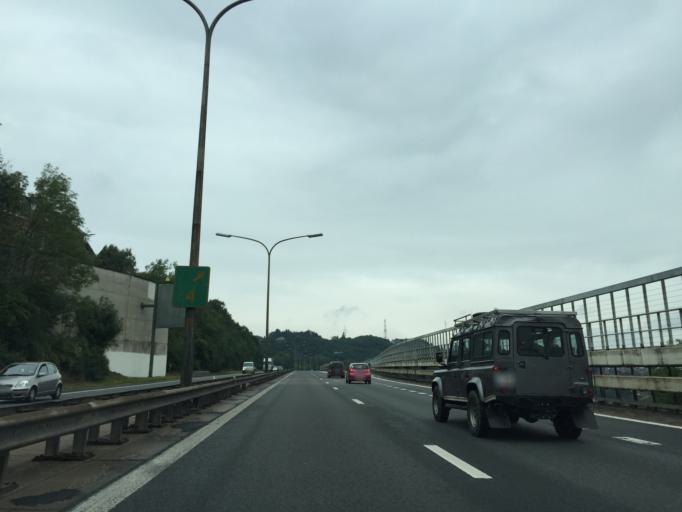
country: BE
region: Wallonia
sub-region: Province de Liege
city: Verviers
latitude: 50.5898
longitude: 5.8444
